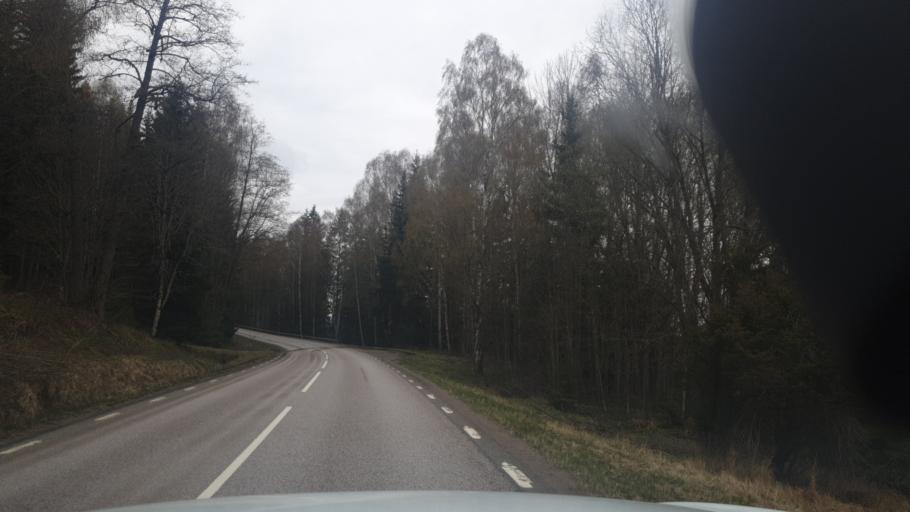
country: SE
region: Vaermland
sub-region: Arvika Kommun
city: Arvika
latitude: 59.4603
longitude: 12.7581
